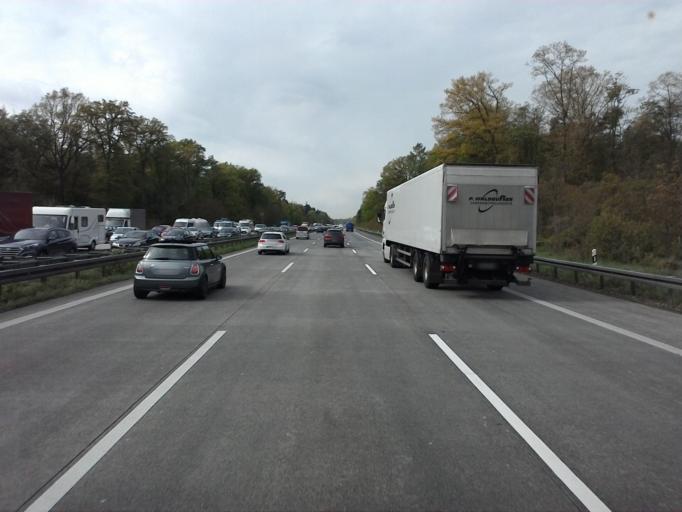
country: DE
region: Baden-Wuerttemberg
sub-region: Karlsruhe Region
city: Weingarten
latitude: 49.0859
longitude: 8.5266
